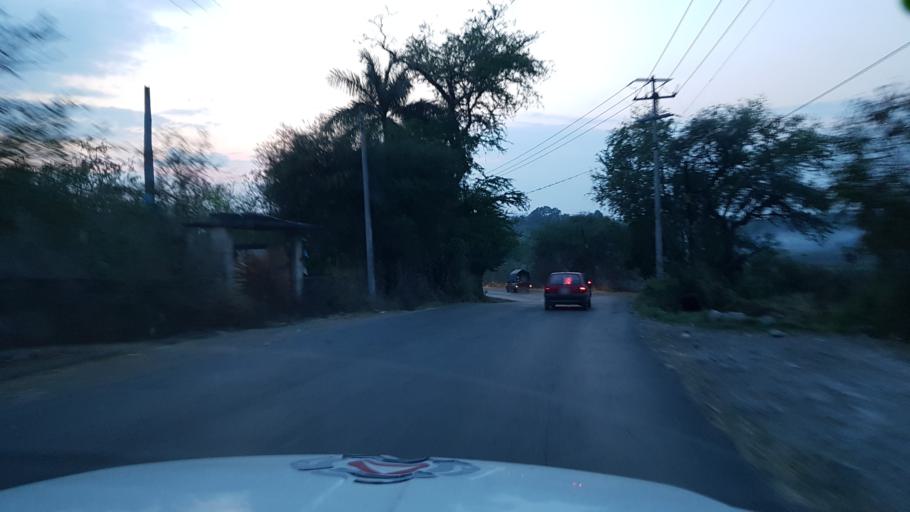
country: MX
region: Morelos
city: Tlaltizapan
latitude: 18.6894
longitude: -99.1266
